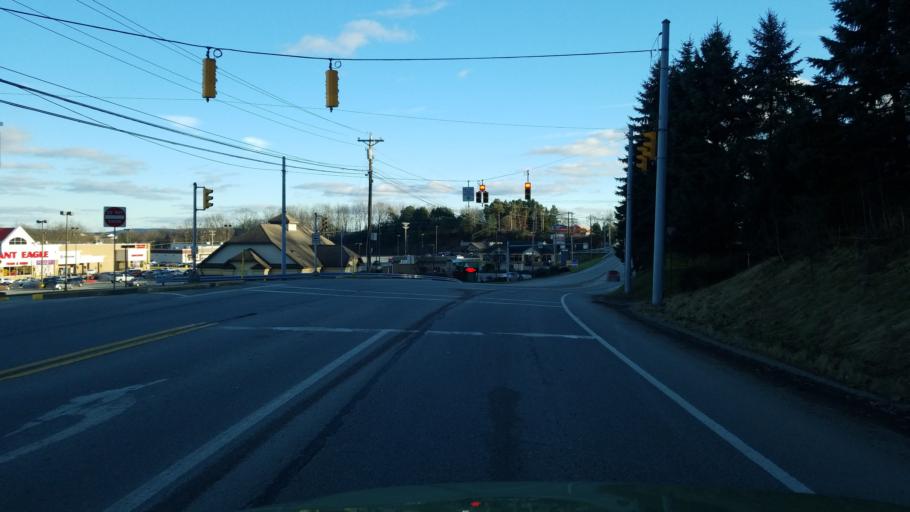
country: US
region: Pennsylvania
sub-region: Indiana County
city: Indiana
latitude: 40.6140
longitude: -79.1914
